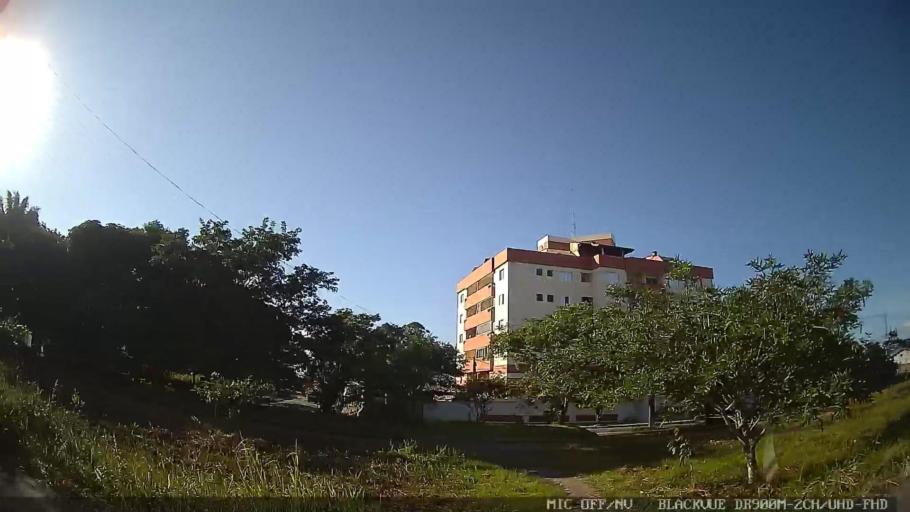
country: BR
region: Sao Paulo
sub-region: Peruibe
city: Peruibe
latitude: -24.2917
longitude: -46.9745
